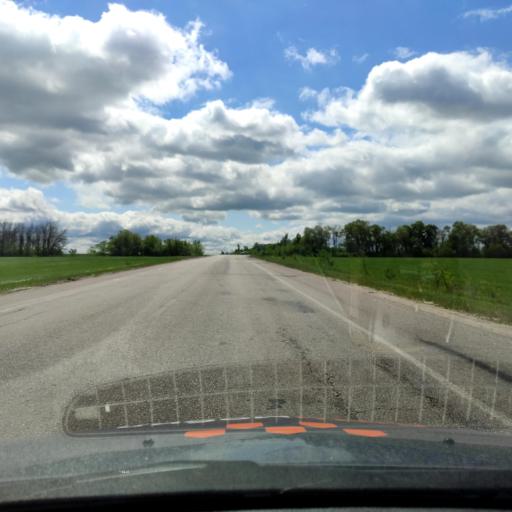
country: RU
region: Voronezj
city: Novaya Usman'
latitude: 51.5915
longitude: 39.3382
